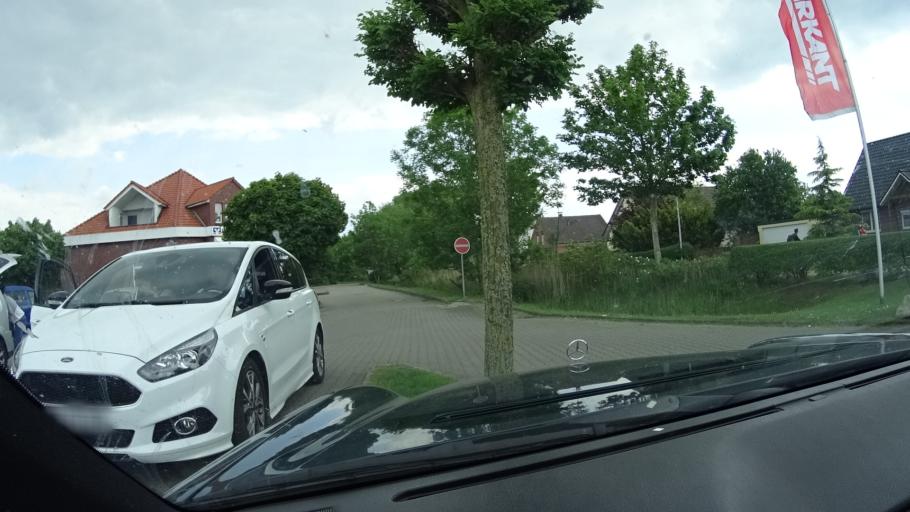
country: DE
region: Lower Saxony
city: Butjadingen
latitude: 53.5725
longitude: 8.2616
